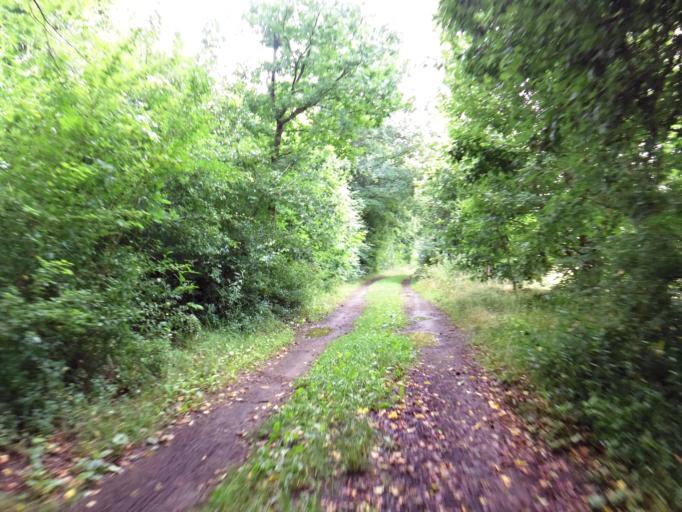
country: DE
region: Saxony
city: Borsdorf
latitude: 51.3451
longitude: 12.5063
